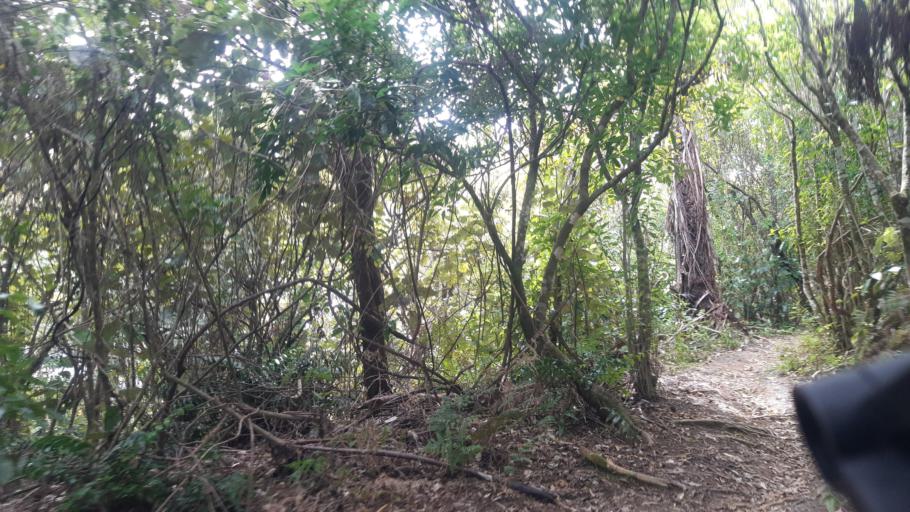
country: NZ
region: Marlborough
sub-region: Marlborough District
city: Picton
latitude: -41.2653
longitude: 173.9991
